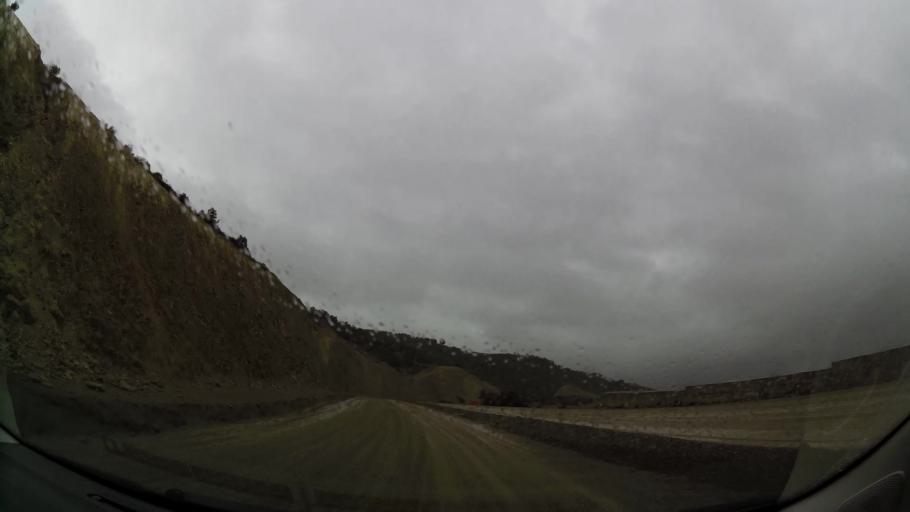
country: MA
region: Taza-Al Hoceima-Taounate
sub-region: Taza
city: Ajdir
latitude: 34.8982
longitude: -3.7825
